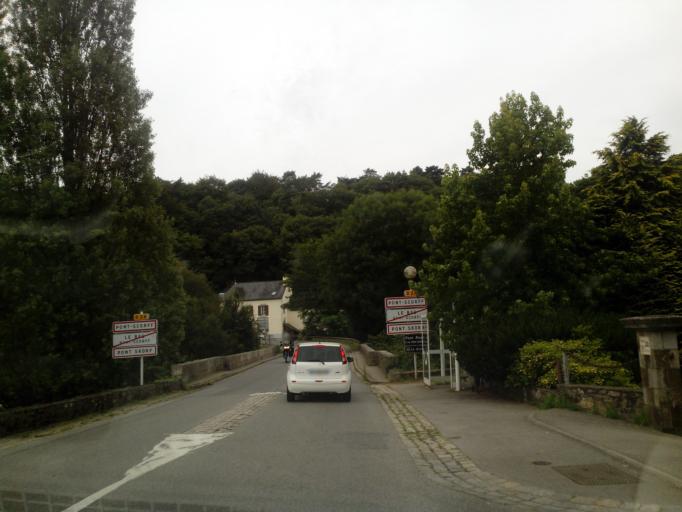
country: FR
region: Brittany
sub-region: Departement du Morbihan
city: Pont-Scorff
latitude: 47.8364
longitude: -3.3933
